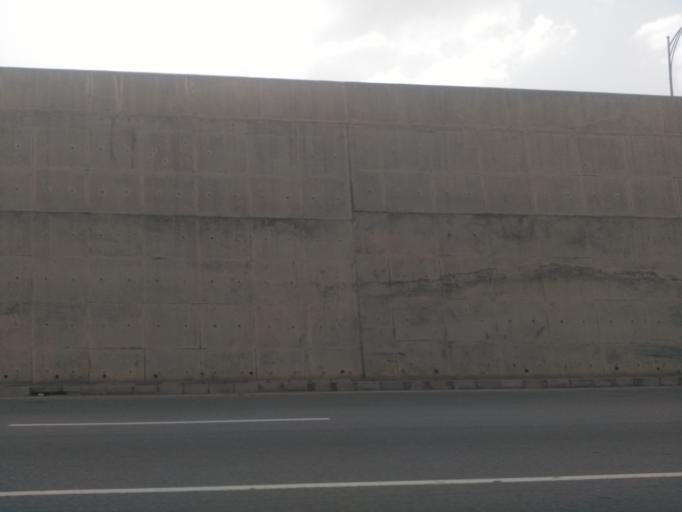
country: GH
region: Greater Accra
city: Dome
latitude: 5.6149
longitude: -0.2151
